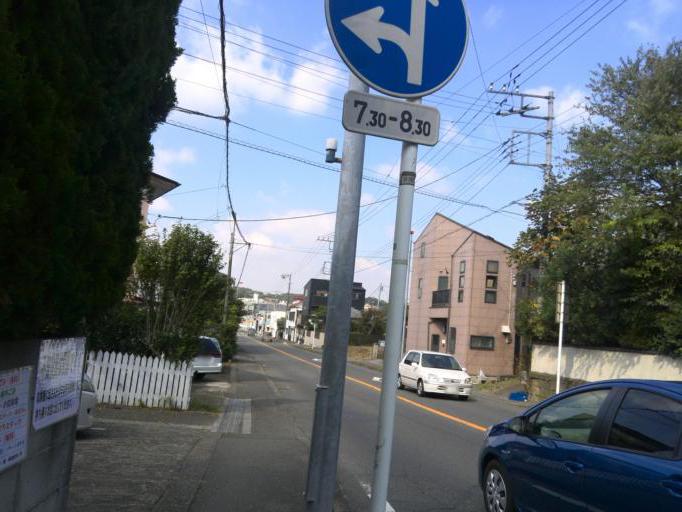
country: JP
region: Kanagawa
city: Zushi
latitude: 35.2898
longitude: 139.5801
